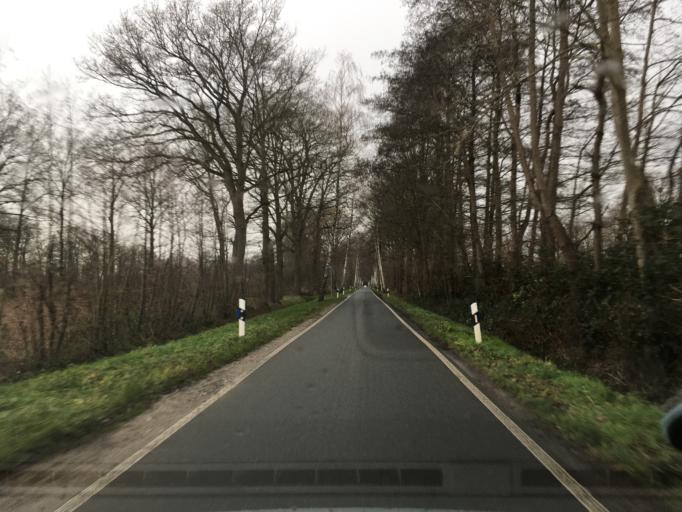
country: DE
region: North Rhine-Westphalia
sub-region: Regierungsbezirk Munster
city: Heek
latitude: 52.1374
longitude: 7.1327
